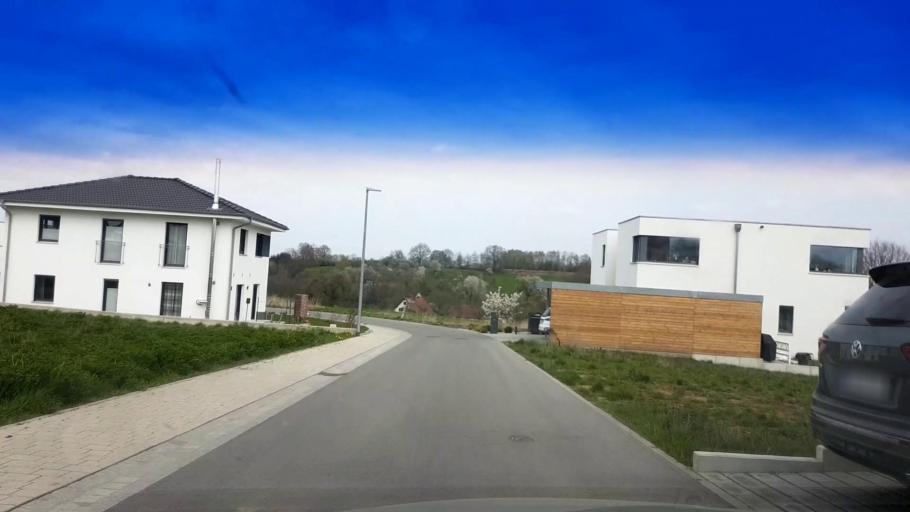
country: DE
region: Bavaria
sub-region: Upper Franconia
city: Bischberg
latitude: 49.9029
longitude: 10.8386
